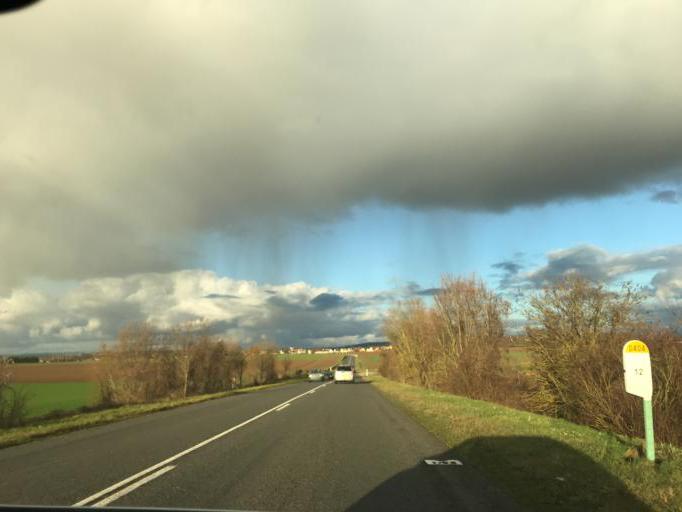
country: FR
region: Ile-de-France
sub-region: Departement de Seine-et-Marne
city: Claye-Souilly
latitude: 48.9557
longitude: 2.6960
